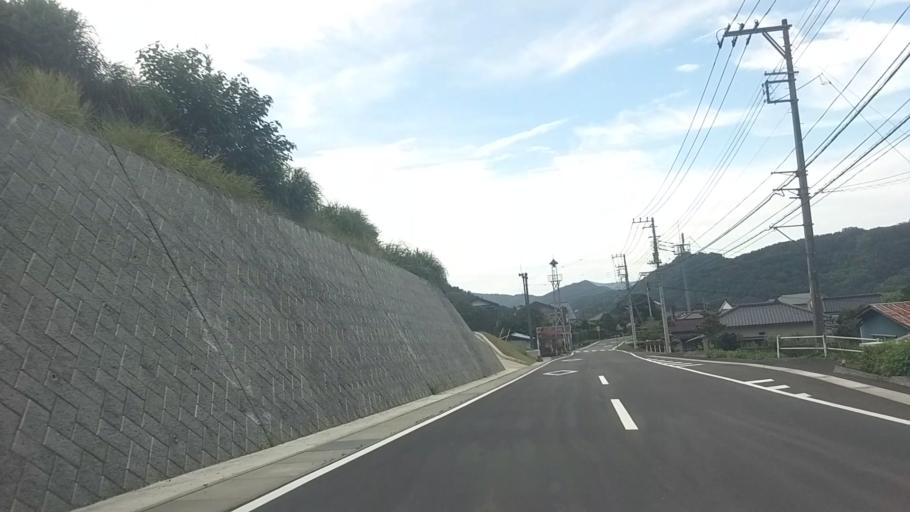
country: JP
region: Shizuoka
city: Ito
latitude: 34.9663
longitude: 138.9706
